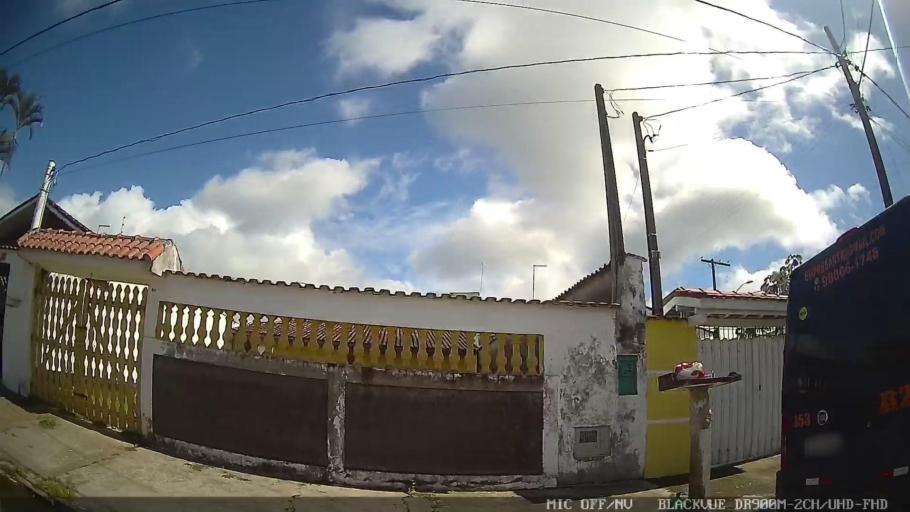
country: BR
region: Sao Paulo
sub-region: Itanhaem
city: Itanhaem
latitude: -24.2446
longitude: -46.8895
